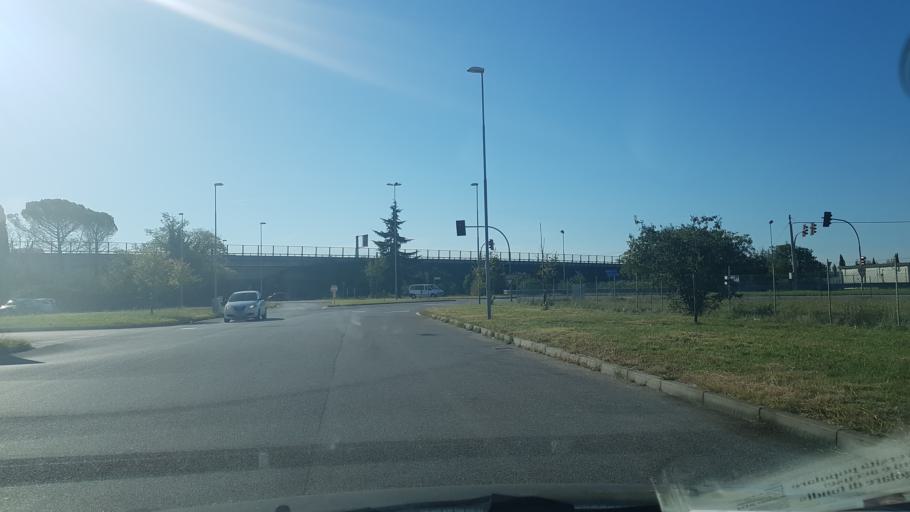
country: IT
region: Friuli Venezia Giulia
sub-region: Provincia di Gorizia
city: Sagrado
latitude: 45.8943
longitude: 13.4722
